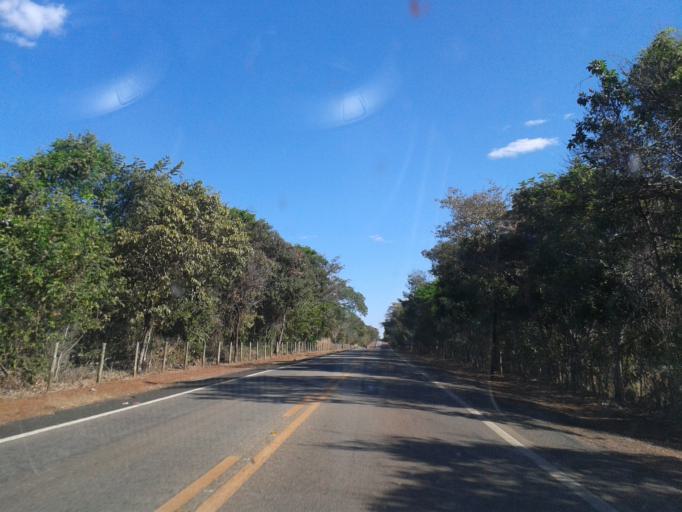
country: BR
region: Goias
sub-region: Mozarlandia
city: Mozarlandia
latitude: -14.6696
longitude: -50.5339
